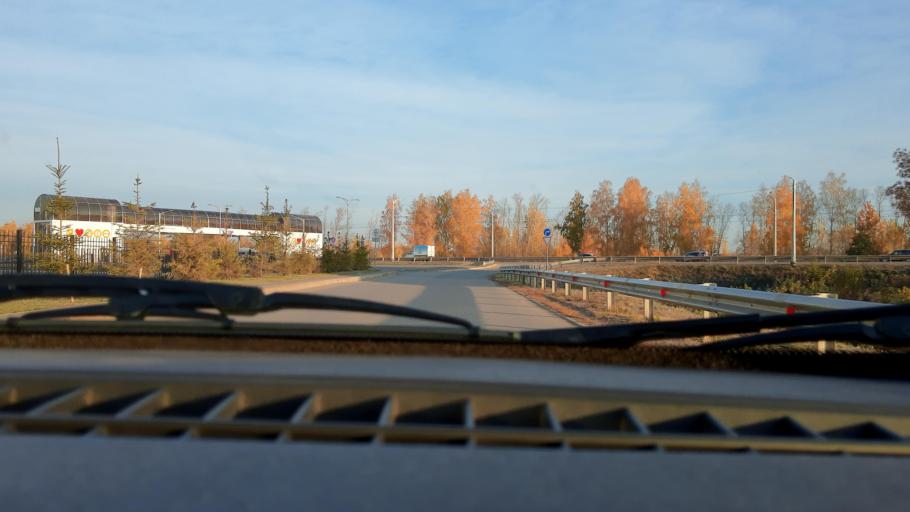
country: RU
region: Bashkortostan
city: Mikhaylovka
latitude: 54.7685
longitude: 55.9146
